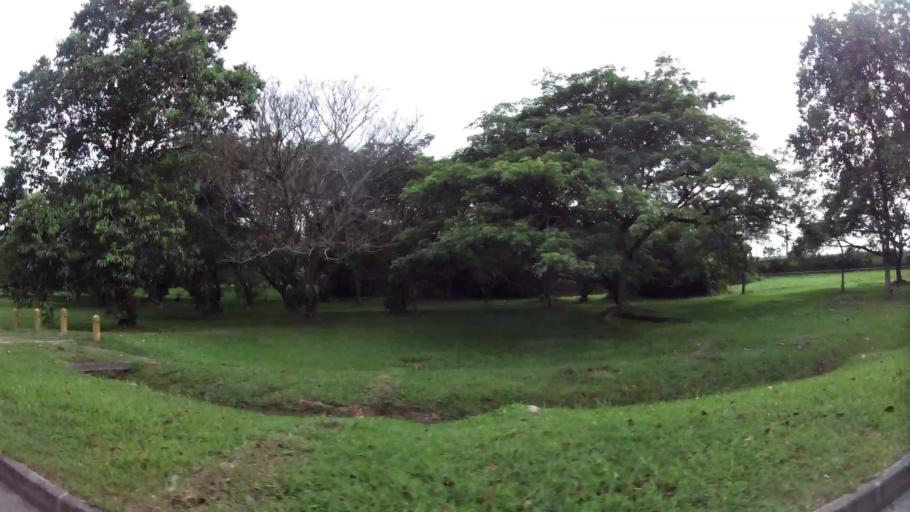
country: MY
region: Johor
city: Johor Bahru
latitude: 1.4386
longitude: 103.7342
